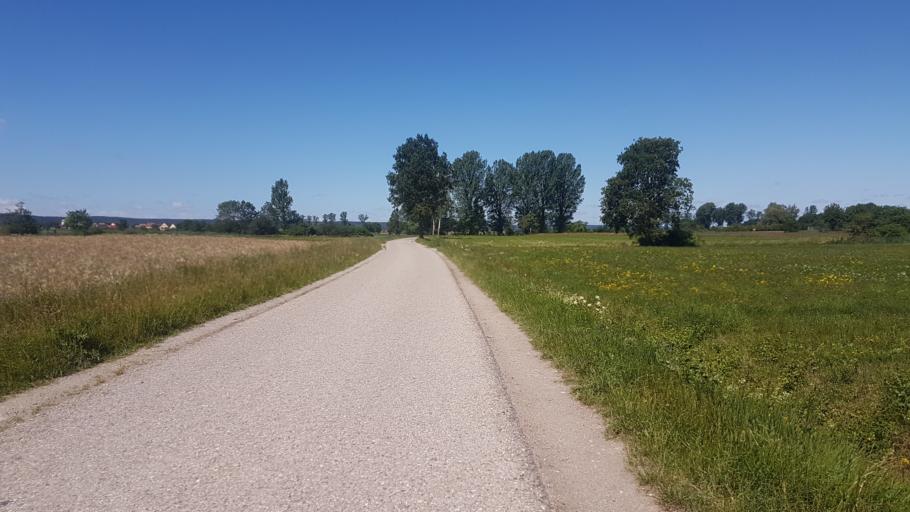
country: DE
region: Bavaria
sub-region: Regierungsbezirk Mittelfranken
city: Herrieden
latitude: 49.2261
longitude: 10.5079
